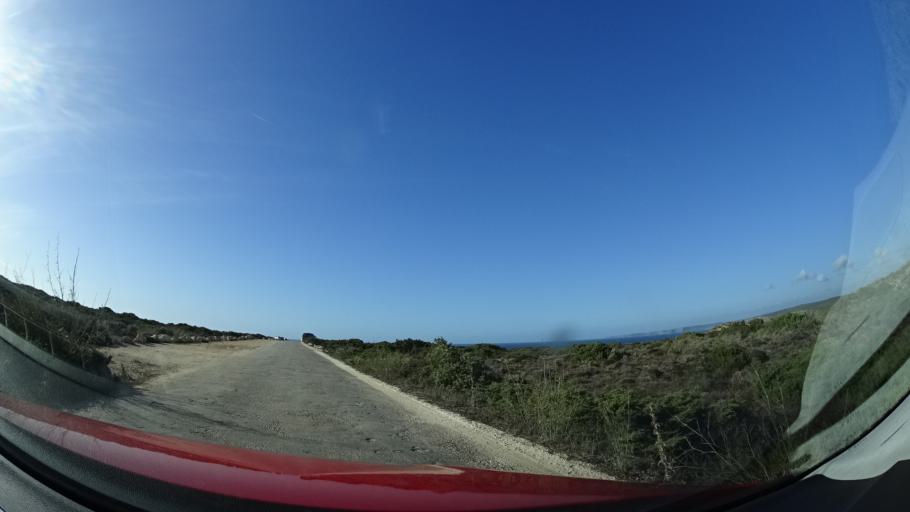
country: PT
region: Faro
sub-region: Vila do Bispo
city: Vila do Bispo
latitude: 37.1951
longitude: -8.9066
